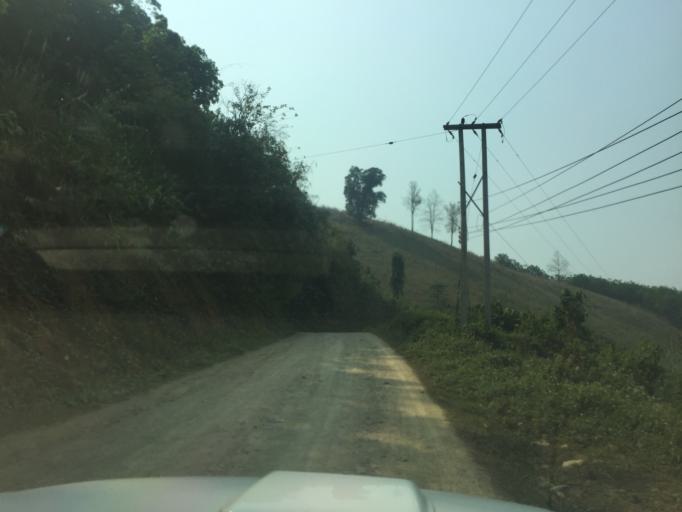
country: TH
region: Phayao
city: Phu Sang
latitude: 19.6199
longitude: 100.5388
